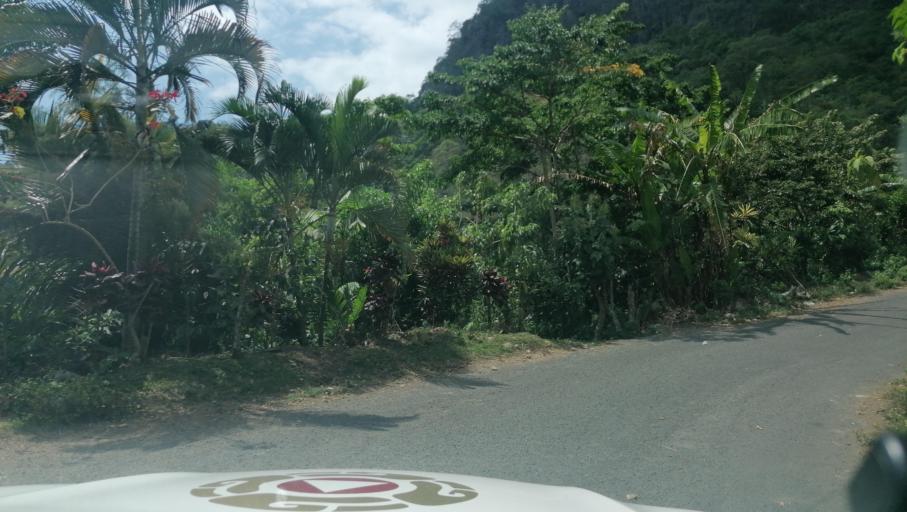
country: MX
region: Chiapas
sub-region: Cacahoatan
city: Benito Juarez
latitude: 15.1129
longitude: -92.2100
